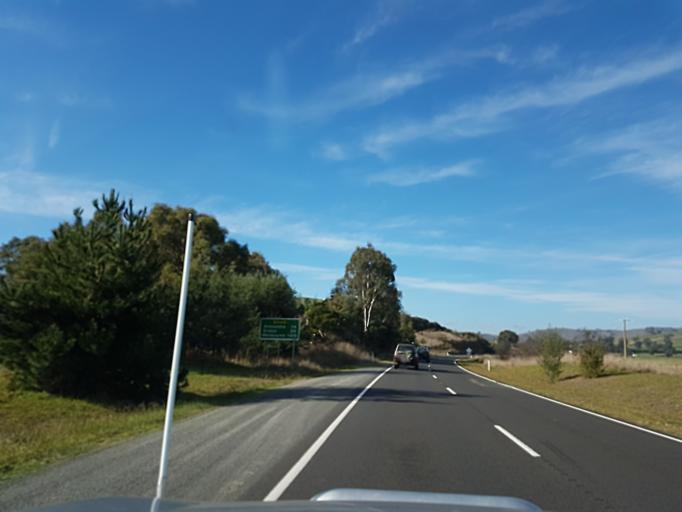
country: AU
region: Victoria
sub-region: Murrindindi
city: Alexandra
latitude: -37.1492
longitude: 145.5863
